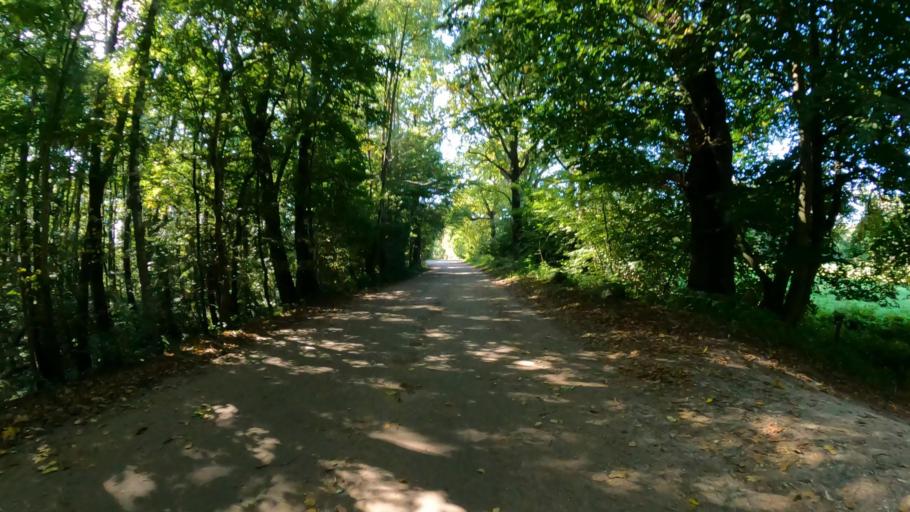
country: DE
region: Schleswig-Holstein
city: Ahrensburg
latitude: 53.6694
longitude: 10.2048
